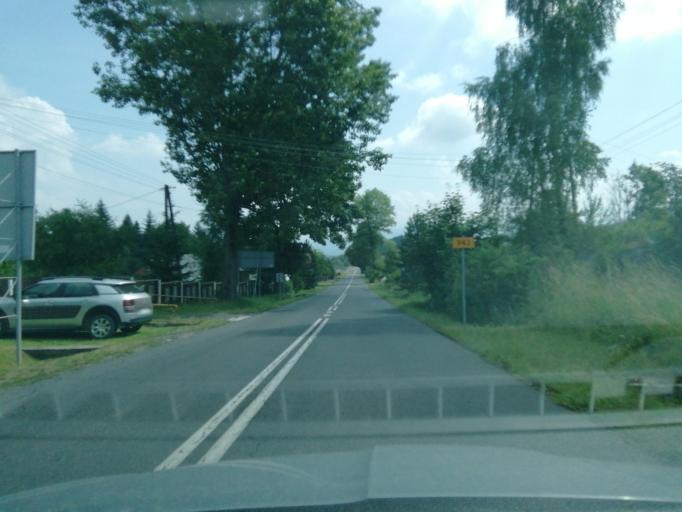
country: PL
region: Silesian Voivodeship
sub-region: Powiat zywiecki
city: Kamesznica
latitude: 49.5486
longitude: 19.0163
